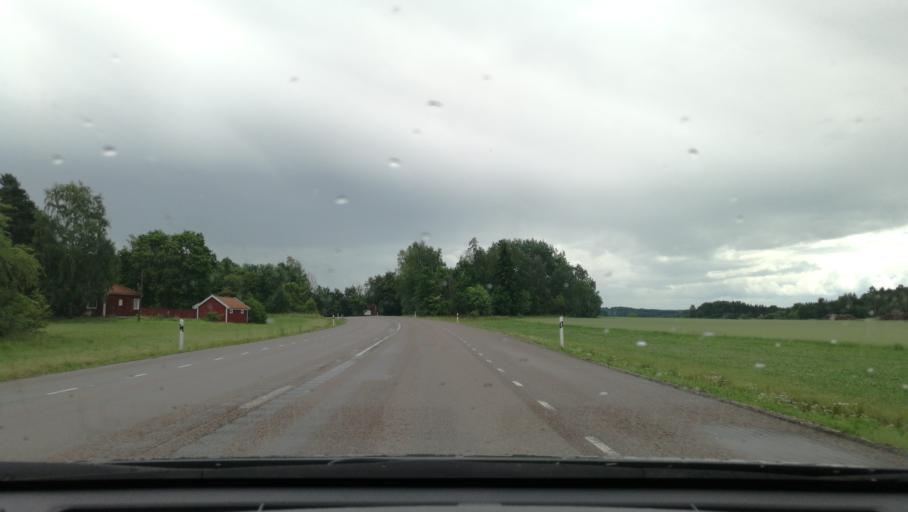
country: SE
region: Vaestmanland
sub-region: Kungsors Kommun
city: Kungsoer
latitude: 59.4443
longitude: 16.0448
